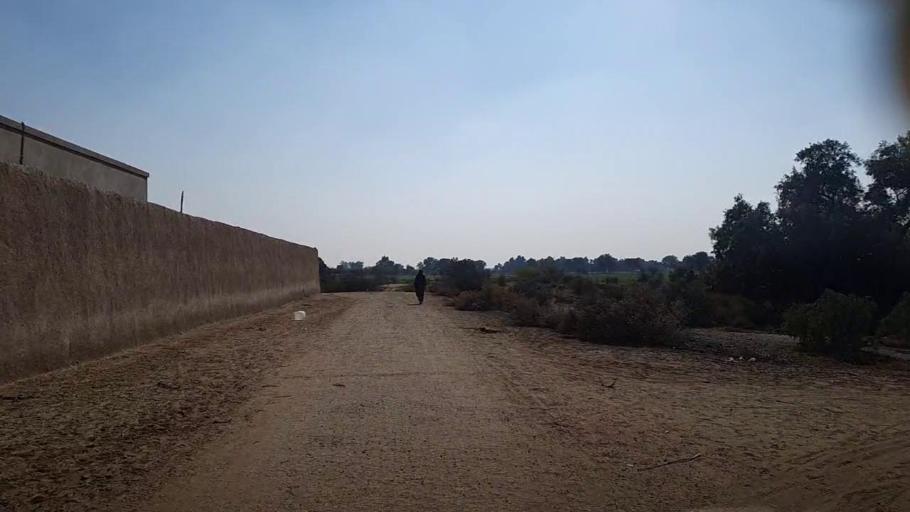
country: PK
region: Sindh
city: Khairpur
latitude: 27.9587
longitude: 69.7292
